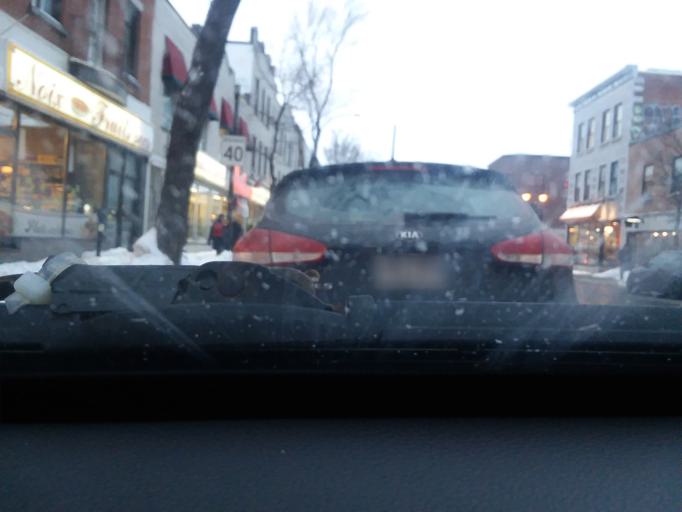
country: CA
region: Quebec
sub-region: Montreal
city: Montreal
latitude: 45.5328
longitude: -73.6142
